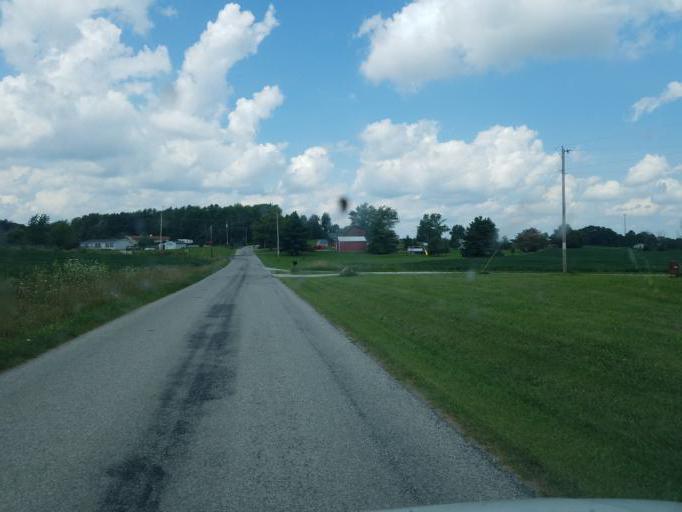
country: US
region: Ohio
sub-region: Knox County
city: Centerburg
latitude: 40.3901
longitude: -82.6756
